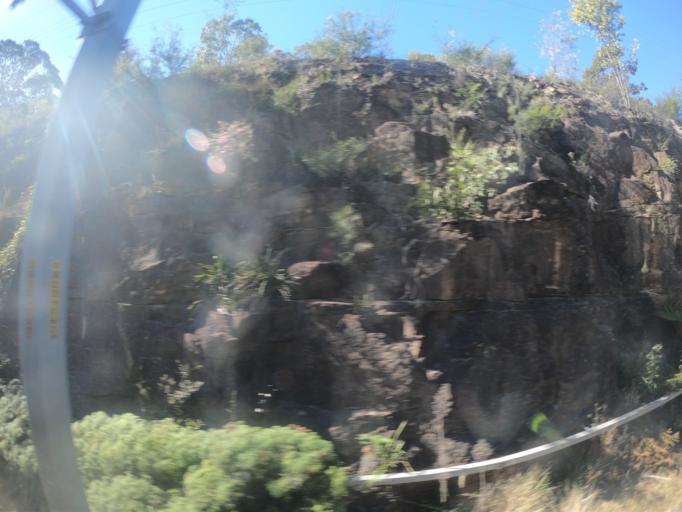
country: AU
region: New South Wales
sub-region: Sutherland Shire
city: Jannali
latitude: -34.0189
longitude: 151.0636
